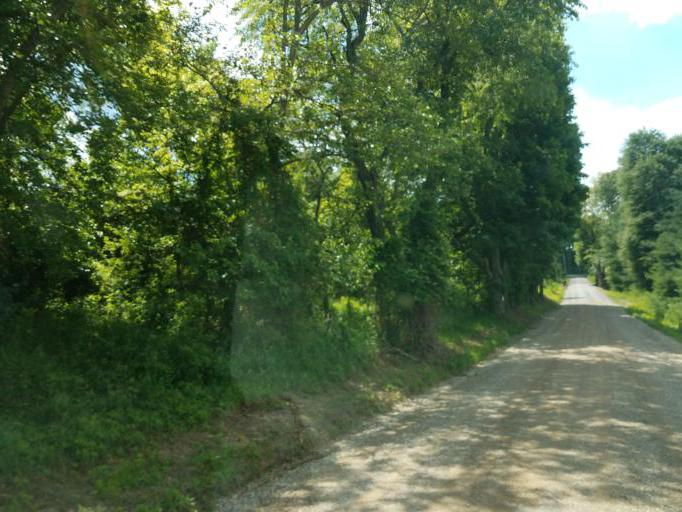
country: US
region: Ohio
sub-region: Knox County
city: Danville
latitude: 40.4099
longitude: -82.2920
